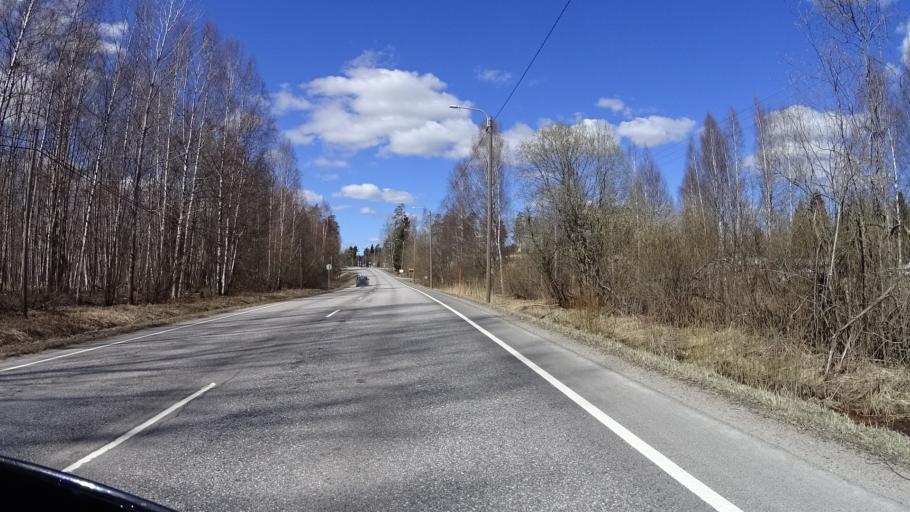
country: FI
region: Uusimaa
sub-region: Helsinki
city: Kirkkonummi
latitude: 60.2667
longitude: 24.4622
